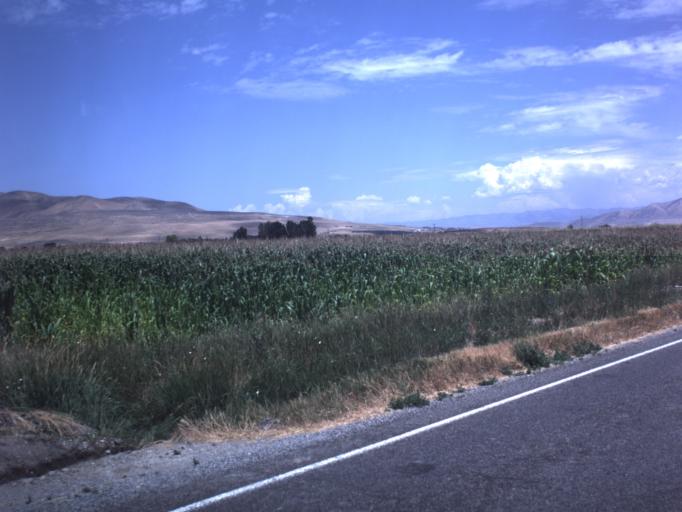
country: US
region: Utah
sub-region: Box Elder County
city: Tremonton
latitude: 41.6946
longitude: -112.2828
